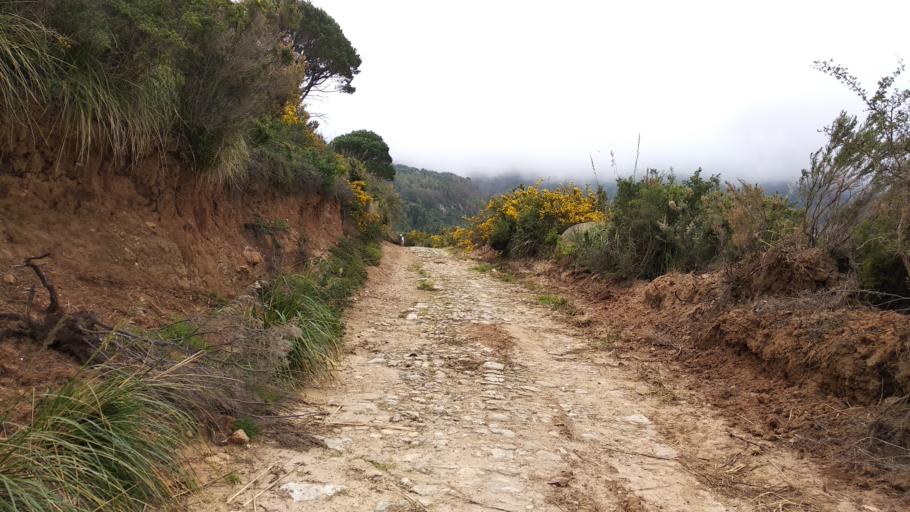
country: IT
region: Sicily
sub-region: Messina
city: Saponara
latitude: 38.2097
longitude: 15.4808
